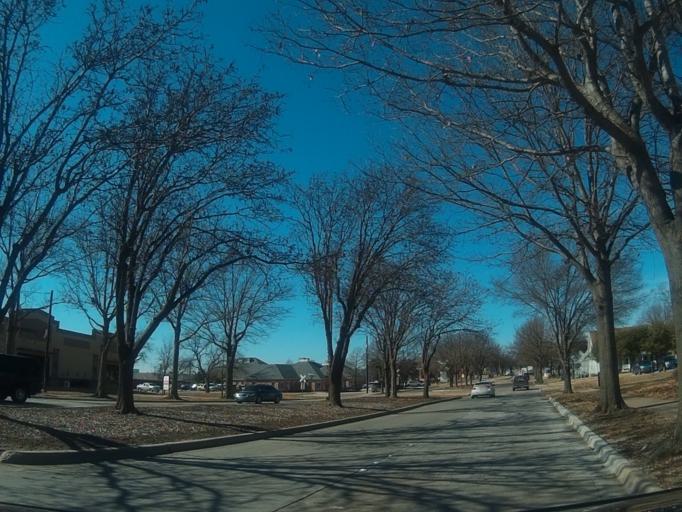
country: US
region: Texas
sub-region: Collin County
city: Allen
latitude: 33.1013
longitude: -96.6698
